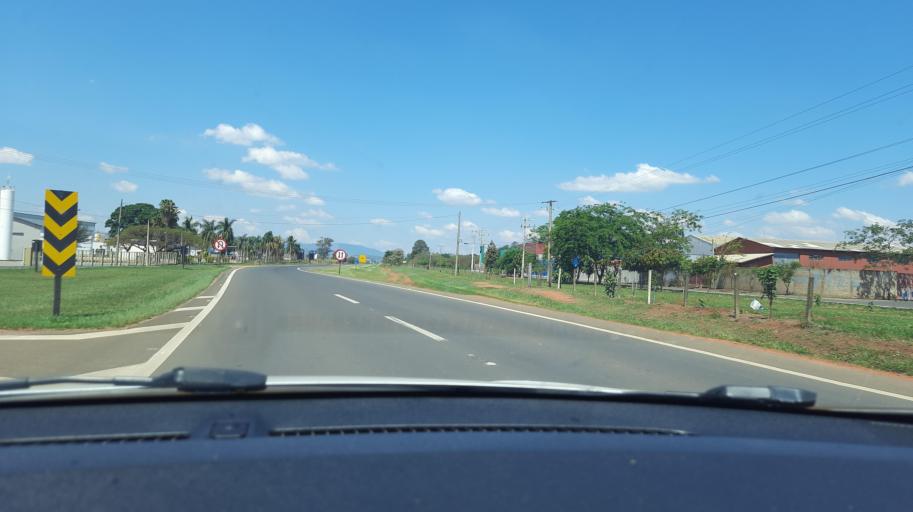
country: BR
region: Sao Paulo
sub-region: Vargem Grande Do Sul
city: Vargem Grande do Sul
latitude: -21.8286
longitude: -46.9410
